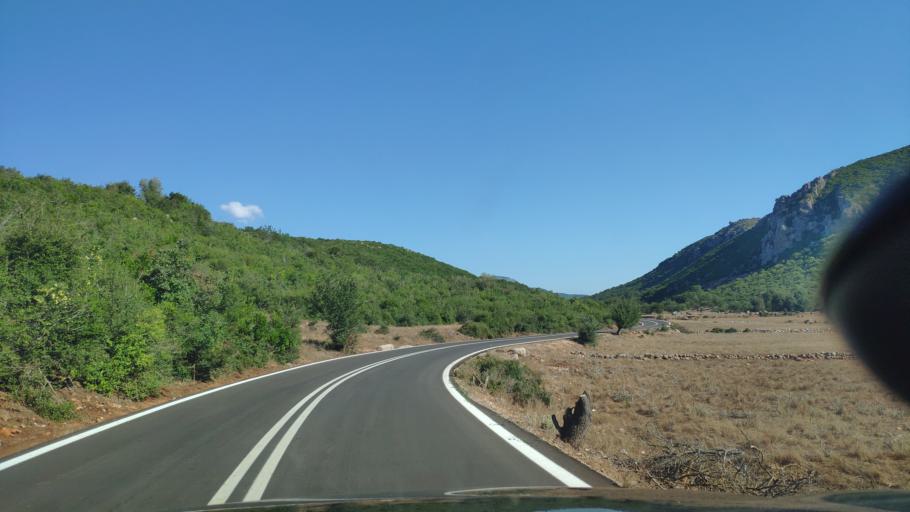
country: GR
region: West Greece
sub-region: Nomos Aitolias kai Akarnanias
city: Fitiai
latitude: 38.6720
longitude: 21.1392
